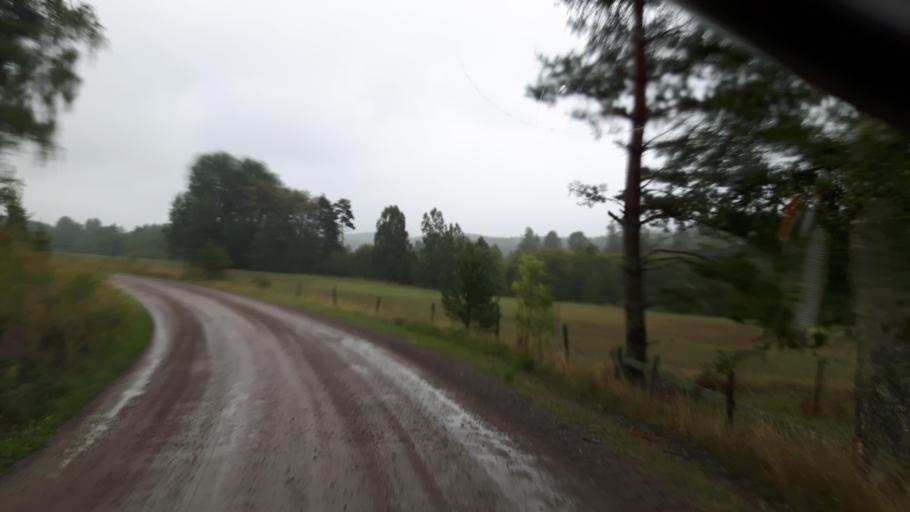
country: SE
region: Kalmar
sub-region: Vimmerby Kommun
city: Sodra Vi
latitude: 57.9088
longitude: 15.9663
